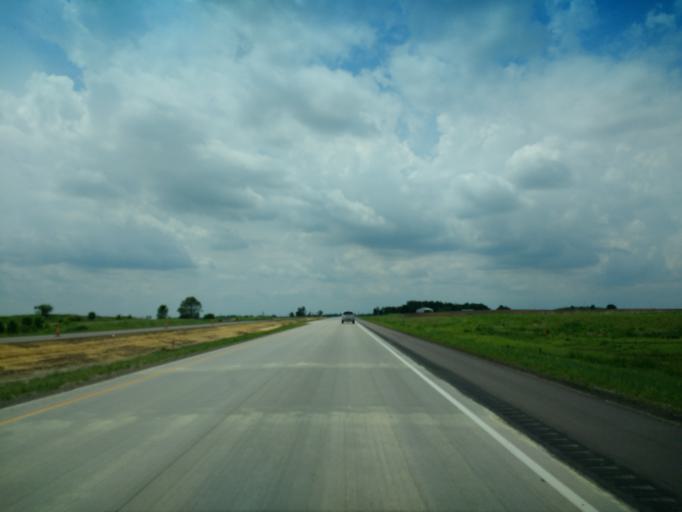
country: US
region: Minnesota
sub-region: Cottonwood County
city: Windom
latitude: 43.8966
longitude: -95.0765
